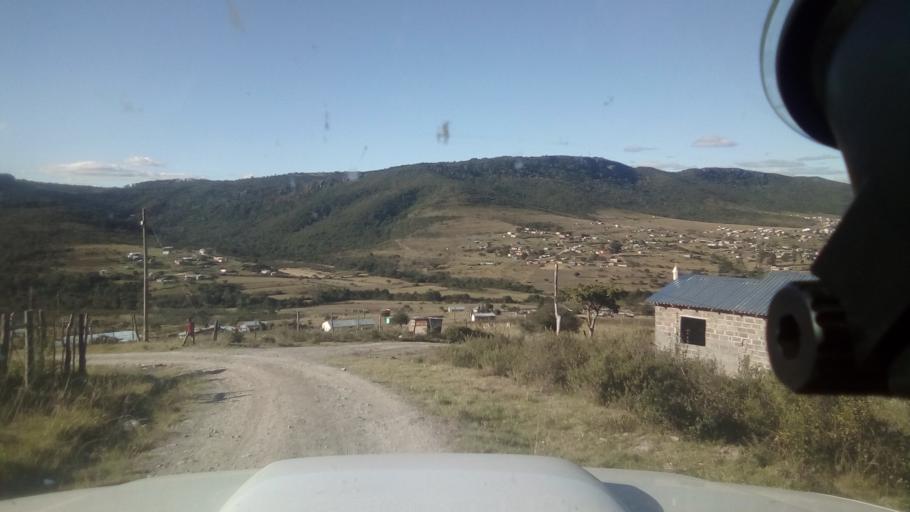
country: ZA
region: Eastern Cape
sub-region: Buffalo City Metropolitan Municipality
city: Bhisho
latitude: -32.7336
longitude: 27.3476
